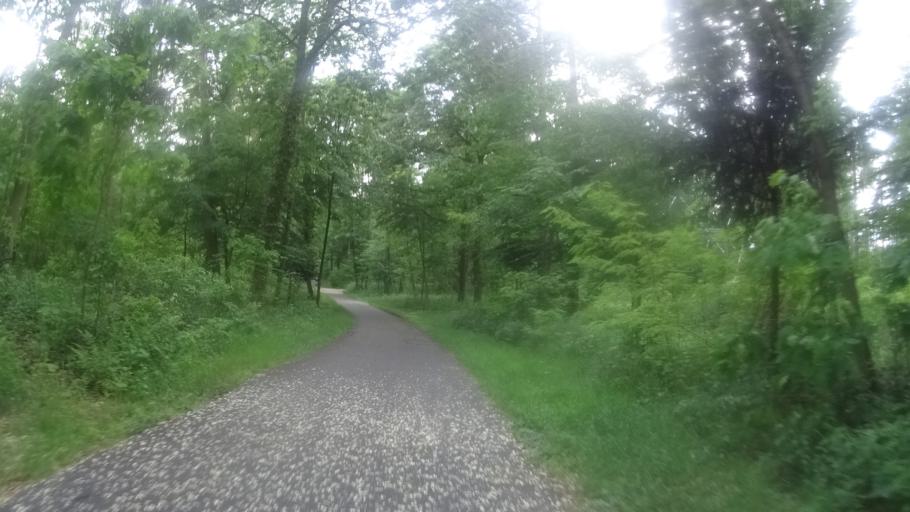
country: DE
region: Baden-Wuerttemberg
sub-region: Karlsruhe Region
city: Rastatt
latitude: 48.8341
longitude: 8.1800
